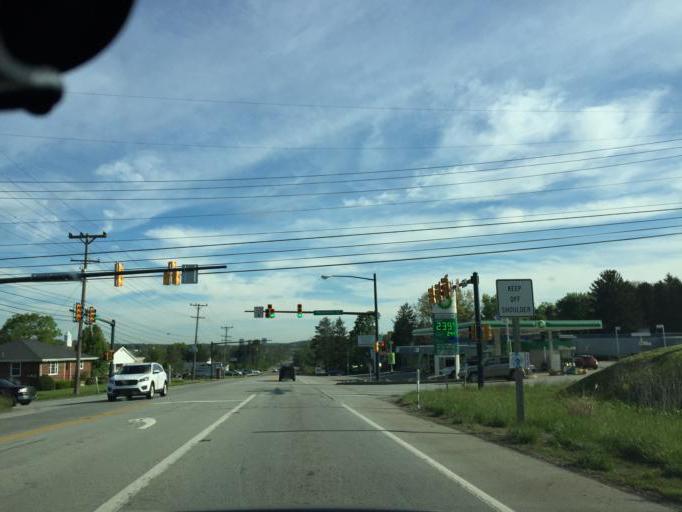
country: US
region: Pennsylvania
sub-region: Westmoreland County
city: Lawson Heights
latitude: 40.2953
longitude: -79.3940
